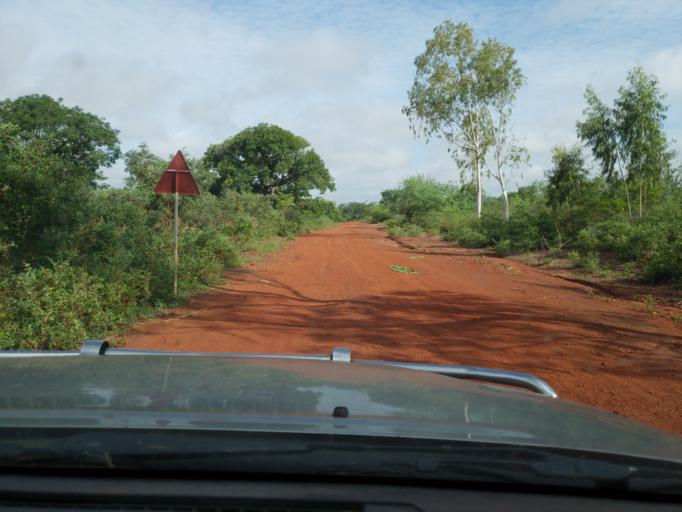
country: ML
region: Sikasso
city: Koutiala
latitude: 12.3908
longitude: -5.9757
